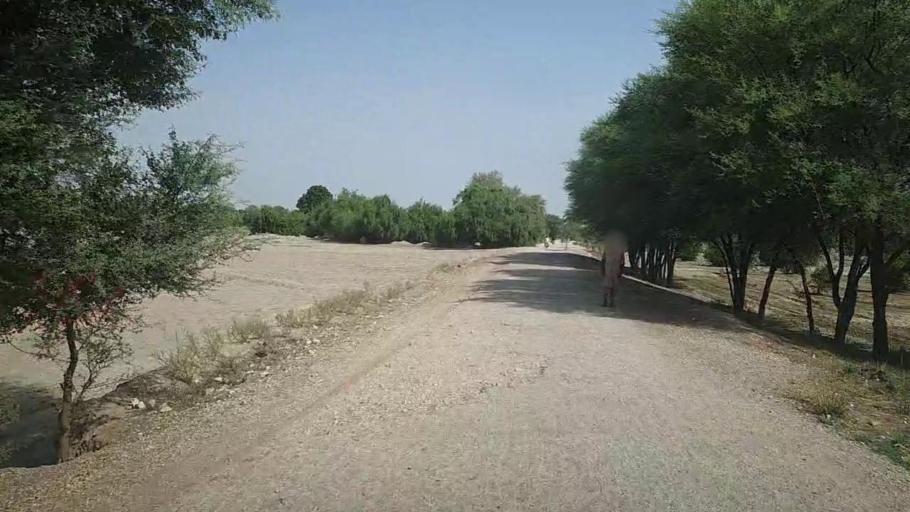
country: PK
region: Sindh
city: Pad Idan
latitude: 26.7609
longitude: 68.3373
